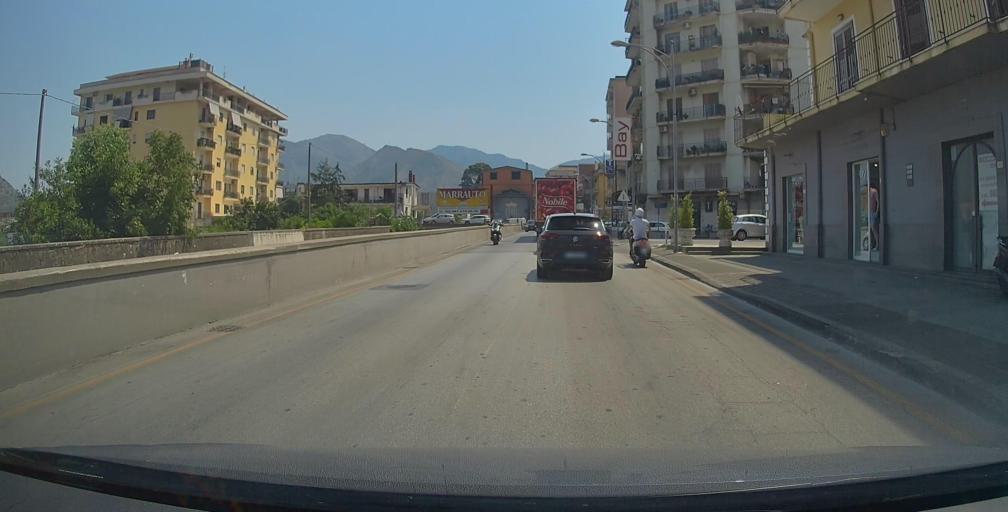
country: IT
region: Campania
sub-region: Provincia di Salerno
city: Nocera Superiore
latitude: 40.7406
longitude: 14.6607
